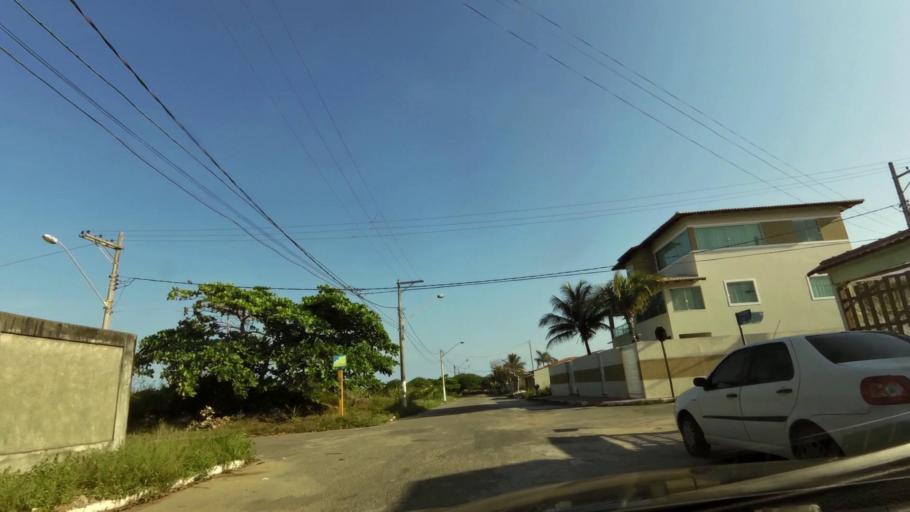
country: BR
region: Espirito Santo
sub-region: Vila Velha
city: Vila Velha
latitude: -20.4880
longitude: -40.3504
